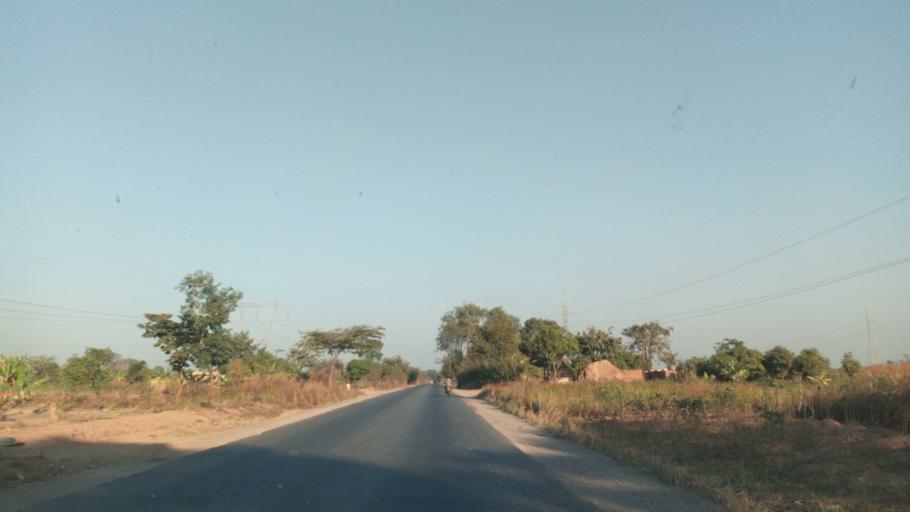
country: CD
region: Katanga
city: Likasi
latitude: -11.1219
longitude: 27.0332
